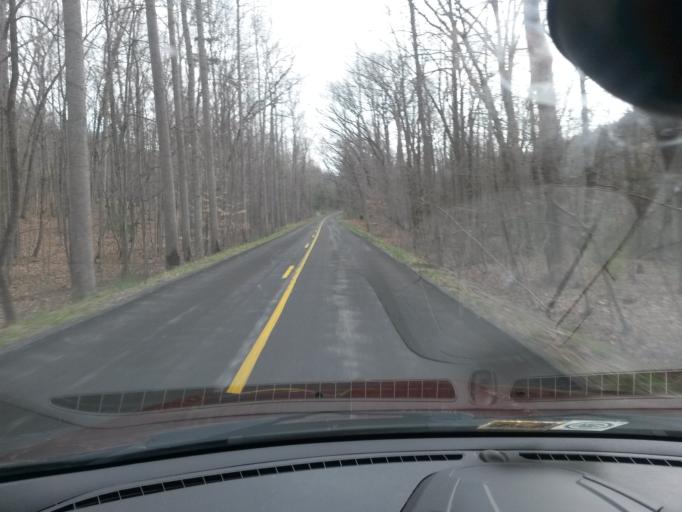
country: US
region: Virginia
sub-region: Alleghany County
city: Clifton Forge
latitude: 37.8306
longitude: -79.6562
